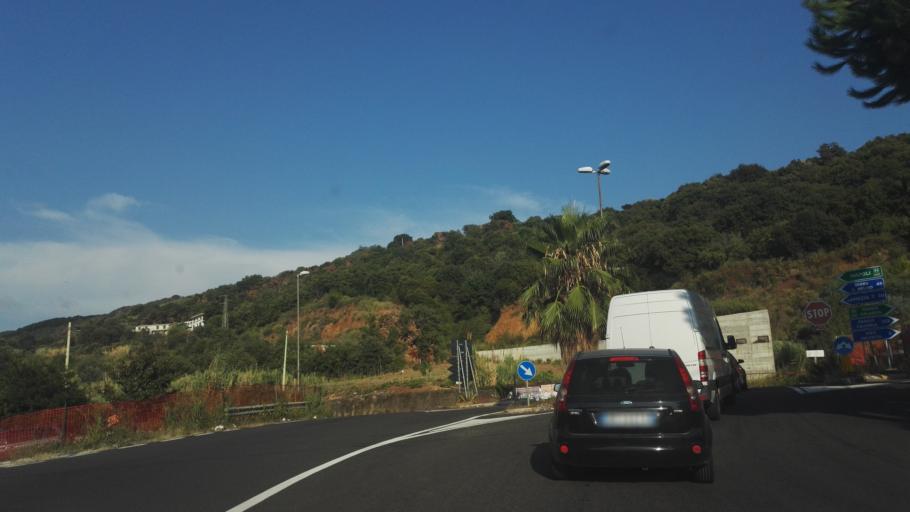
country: IT
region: Calabria
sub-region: Provincia di Vibo-Valentia
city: Sant'Onofrio
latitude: 38.7157
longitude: 16.1430
